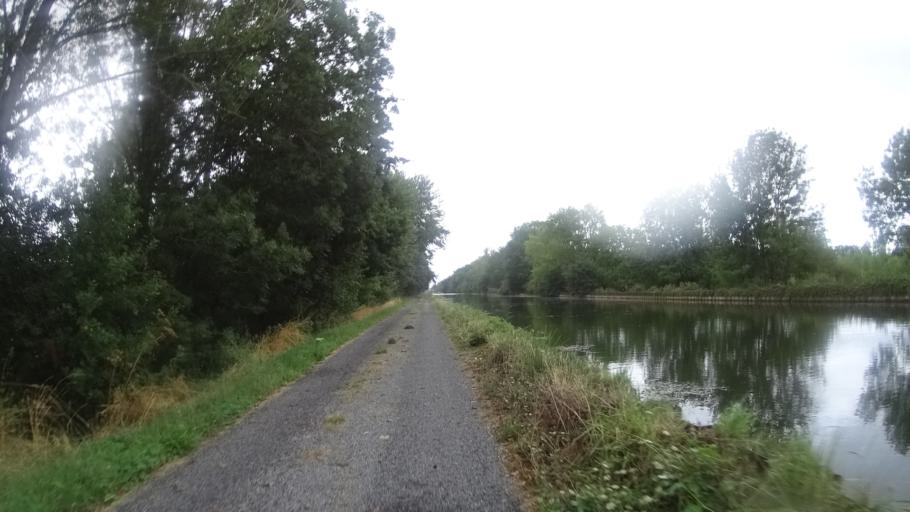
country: FR
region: Picardie
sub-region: Departement de l'Aisne
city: Ribemont
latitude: 49.8114
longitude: 3.4596
